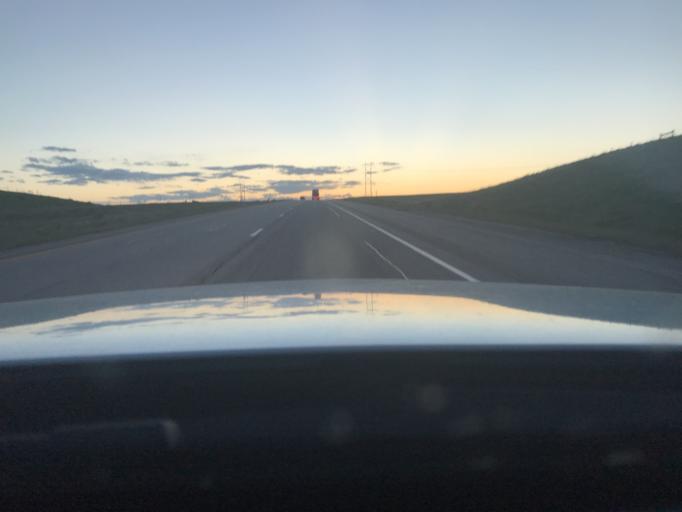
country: US
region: Wyoming
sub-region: Converse County
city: Glenrock
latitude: 42.8283
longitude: -105.8262
